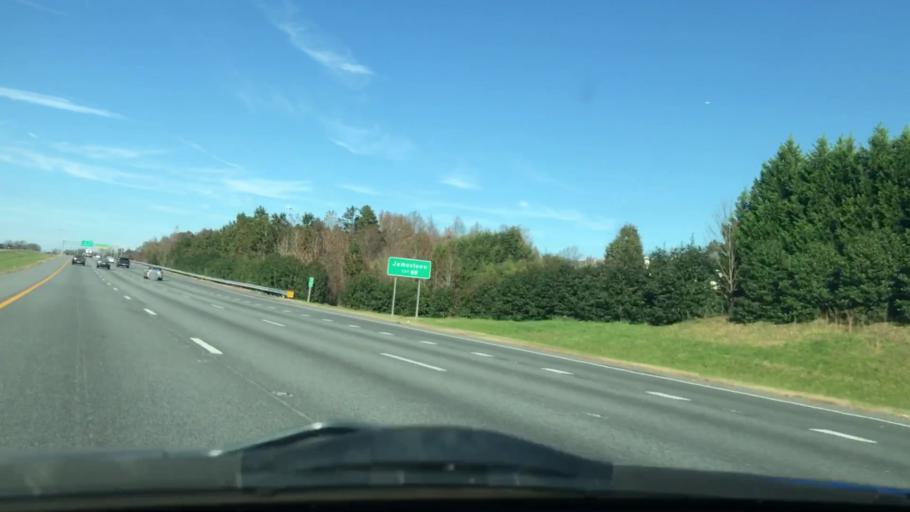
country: US
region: North Carolina
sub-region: Guilford County
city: High Point
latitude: 35.9750
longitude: -79.9742
